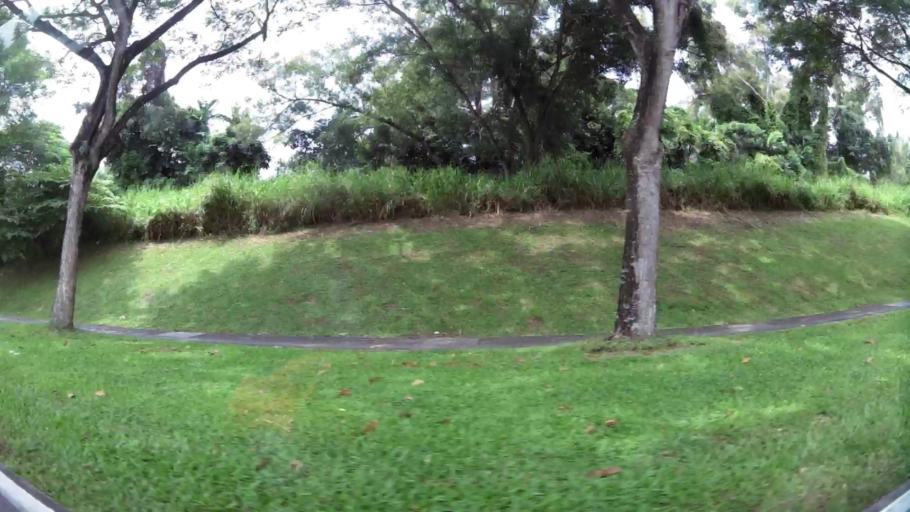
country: SG
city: Singapore
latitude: 1.3475
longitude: 103.9224
